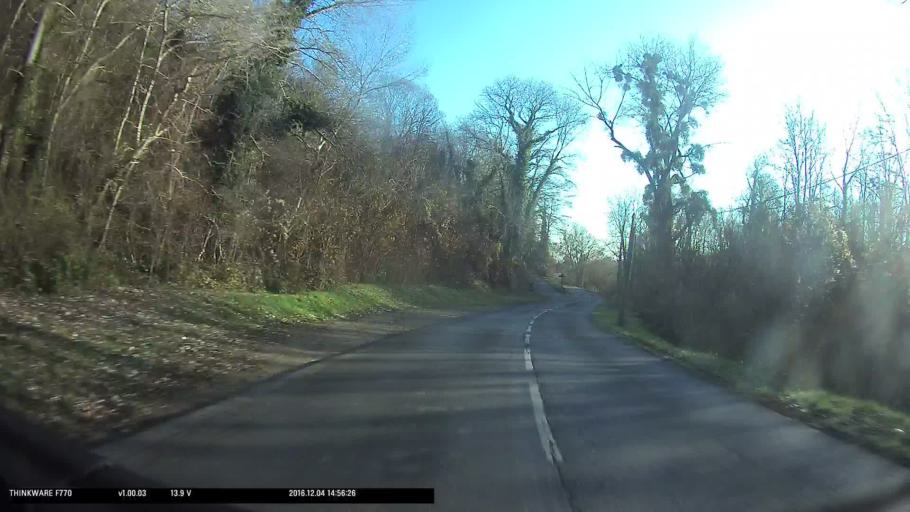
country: FR
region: Ile-de-France
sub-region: Departement du Val-d'Oise
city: Ableiges
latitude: 49.0846
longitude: 1.9987
